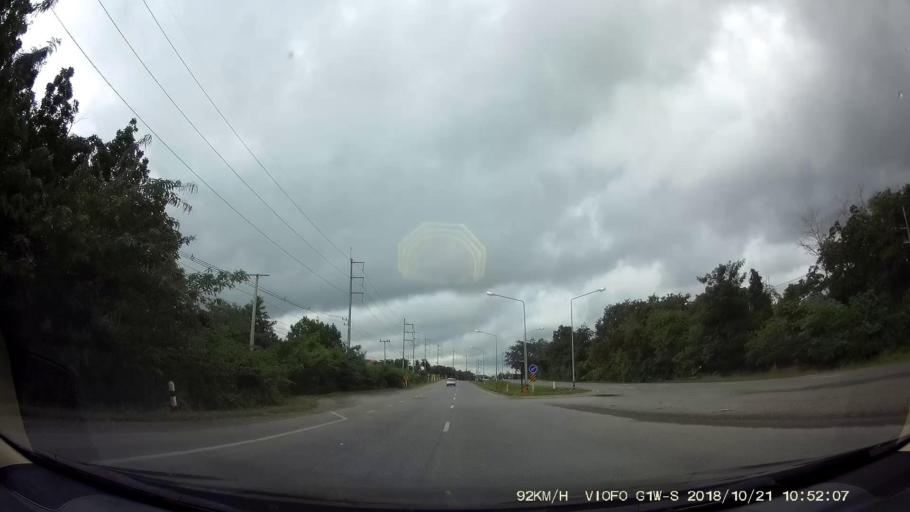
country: TH
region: Chaiyaphum
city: Khon Sawan
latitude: 15.9793
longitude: 102.1969
